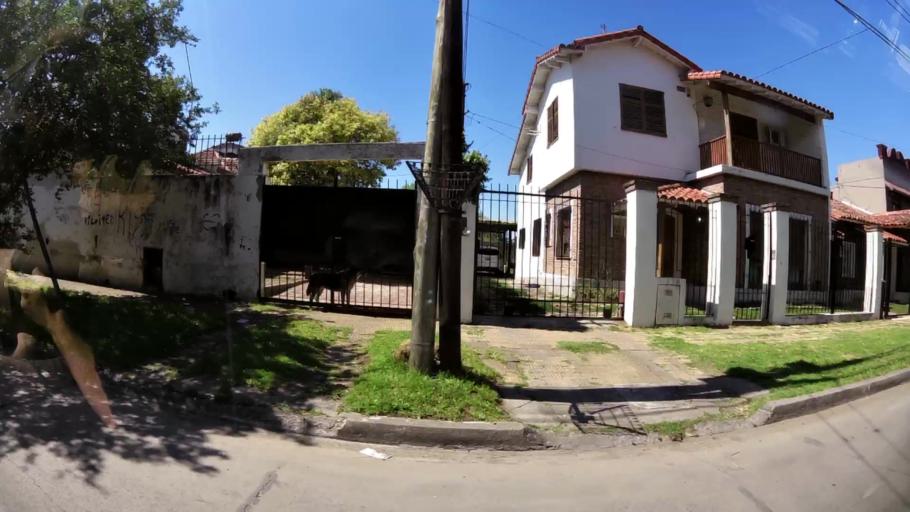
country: AR
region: Buenos Aires
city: Ituzaingo
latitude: -34.6620
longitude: -58.6633
